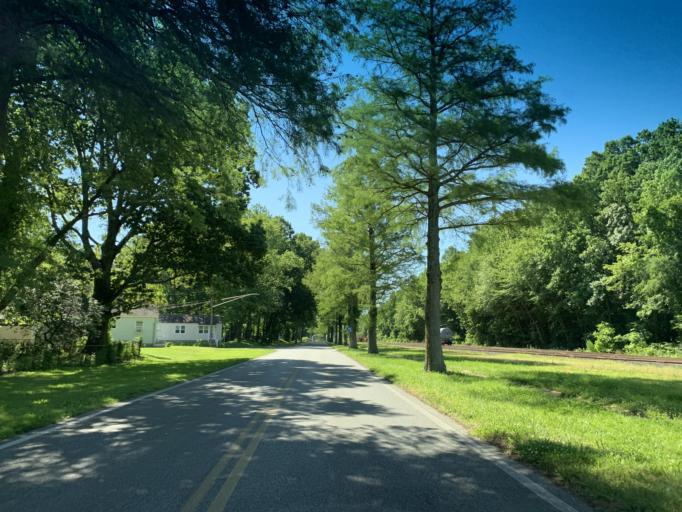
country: US
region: Maryland
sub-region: Harford County
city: Aberdeen
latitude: 39.5011
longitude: -76.1633
